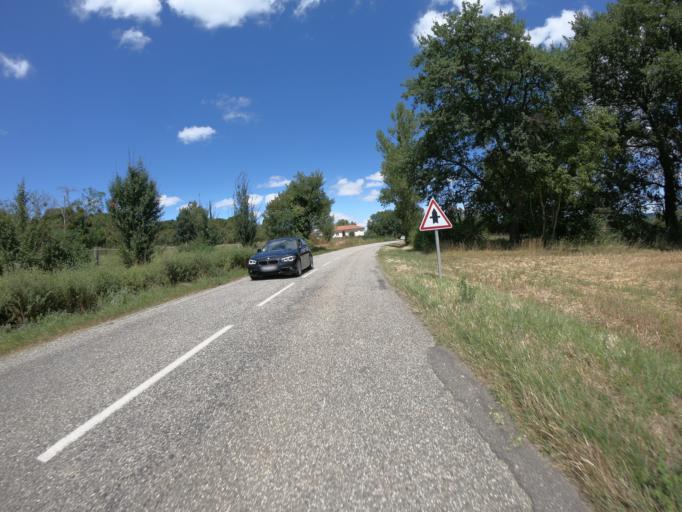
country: FR
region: Midi-Pyrenees
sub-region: Departement de l'Ariege
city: Verniolle
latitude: 43.0775
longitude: 1.7394
